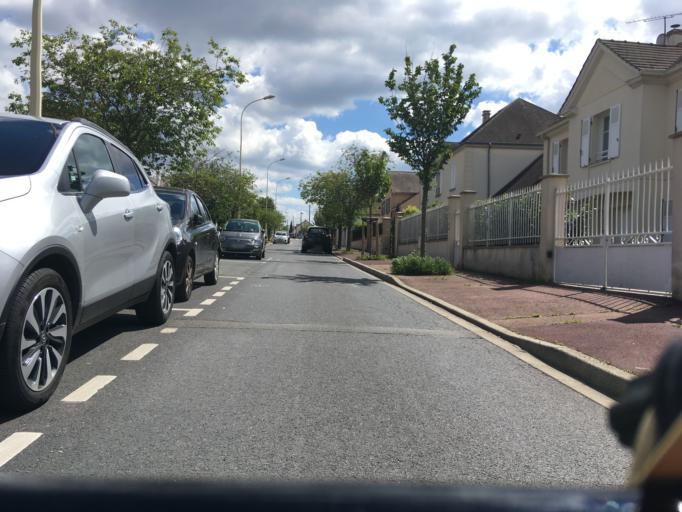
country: FR
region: Ile-de-France
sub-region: Departement des Yvelines
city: Montesson
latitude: 48.9092
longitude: 2.1398
